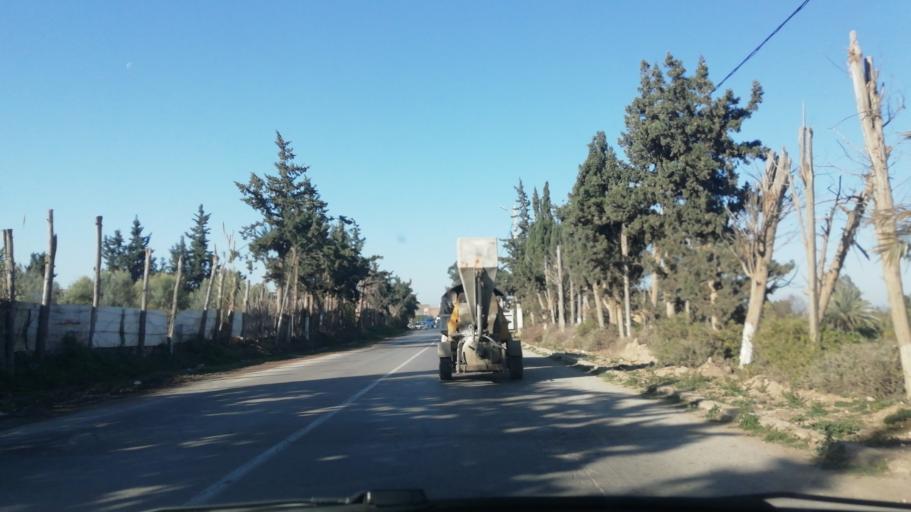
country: DZ
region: Mascara
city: Sig
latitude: 35.5650
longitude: -0.0856
